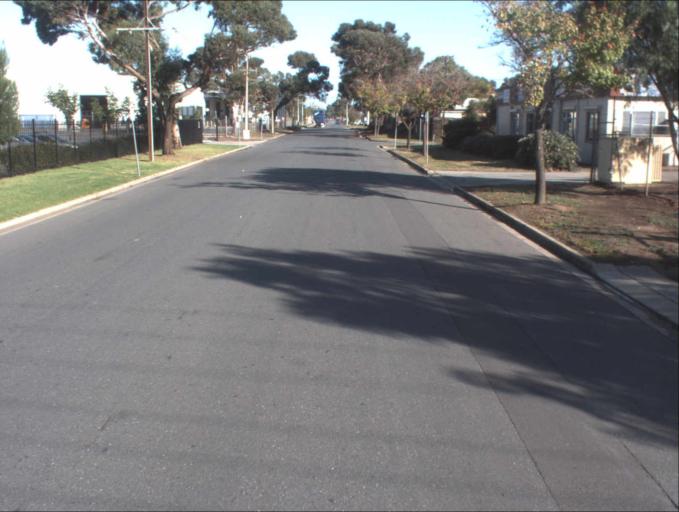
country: AU
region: South Australia
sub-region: Charles Sturt
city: Woodville North
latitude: -34.8454
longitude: 138.5570
